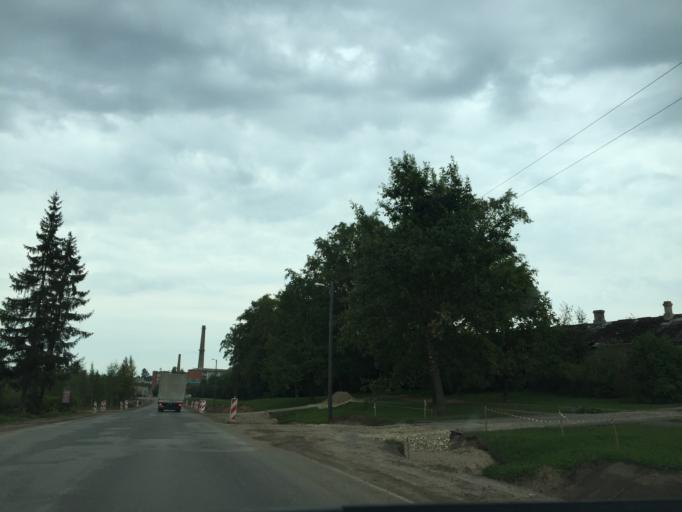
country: LV
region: Ludzas Rajons
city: Ludza
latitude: 56.5353
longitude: 27.6975
